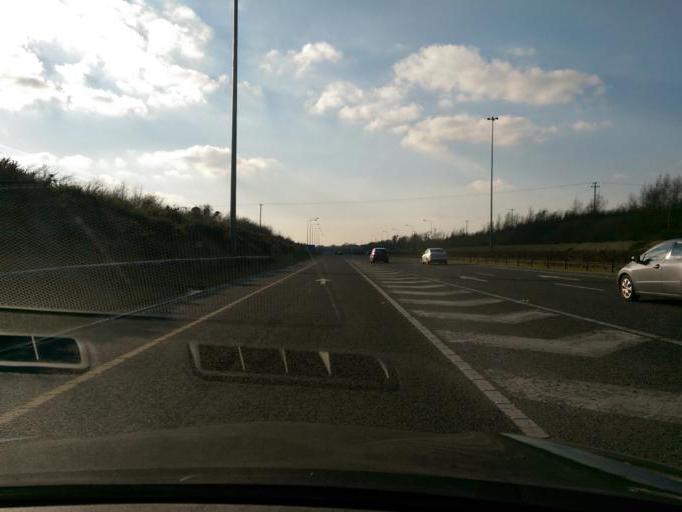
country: IE
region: Leinster
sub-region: Kildare
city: Kildare
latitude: 53.1525
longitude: -6.9246
